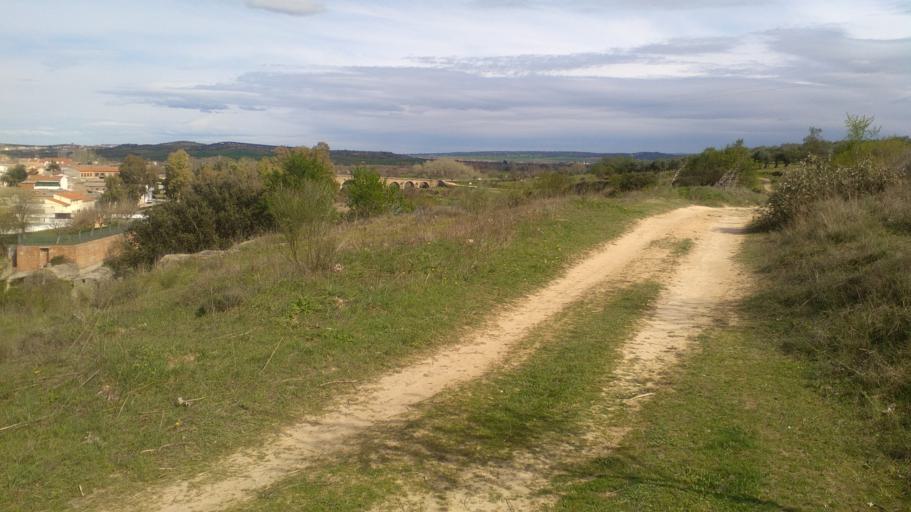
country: ES
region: Castille-La Mancha
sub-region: Province of Toledo
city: El Puente del Arzobispo
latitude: 39.7983
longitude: -5.1767
